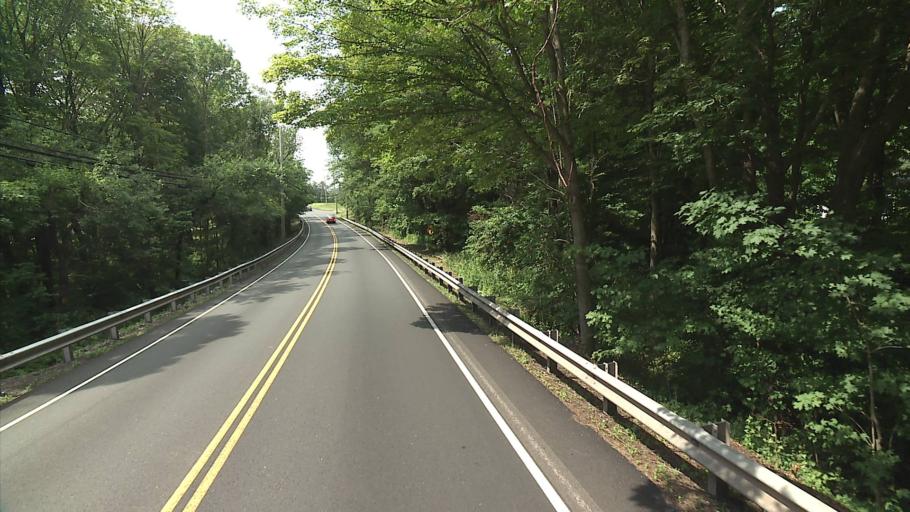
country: US
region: Connecticut
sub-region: New Haven County
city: North Branford
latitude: 41.3864
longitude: -72.7941
